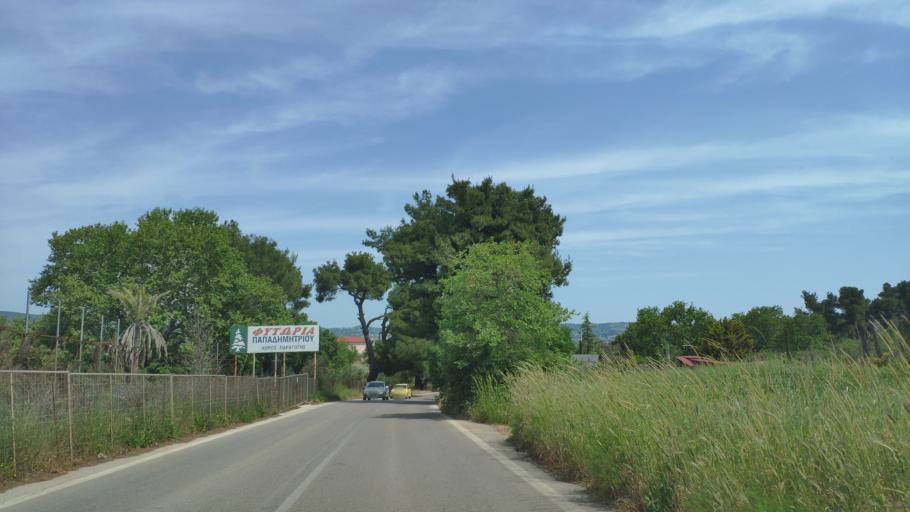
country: GR
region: Attica
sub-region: Nomarchia Anatolikis Attikis
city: Agios Stefanos
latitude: 38.1667
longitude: 23.8612
